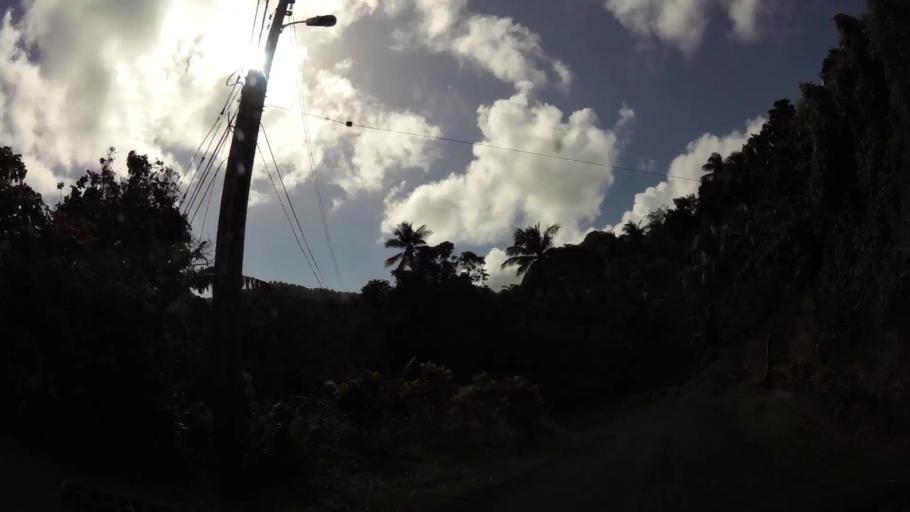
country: DM
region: Saint Andrew
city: Marigot
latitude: 15.5147
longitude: -61.2711
